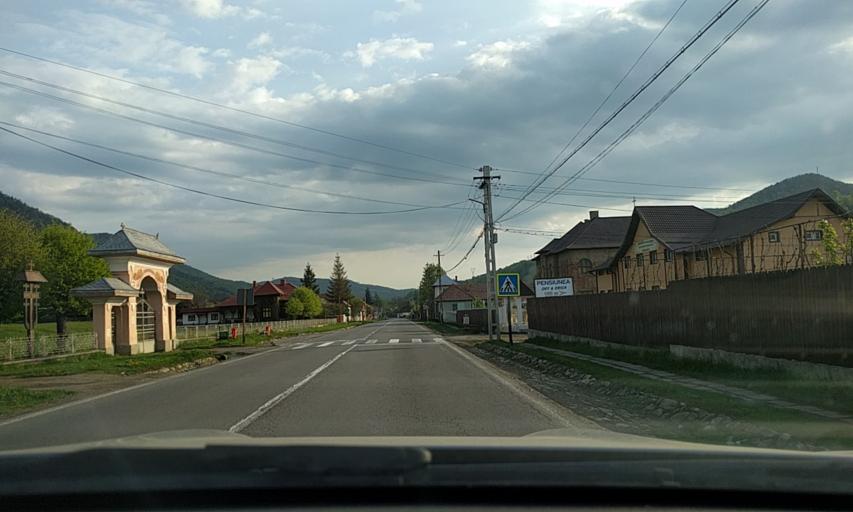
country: RO
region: Bacau
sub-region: Oras Slanic-Moldova
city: Slanic-Moldova
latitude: 46.1423
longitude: 26.4549
